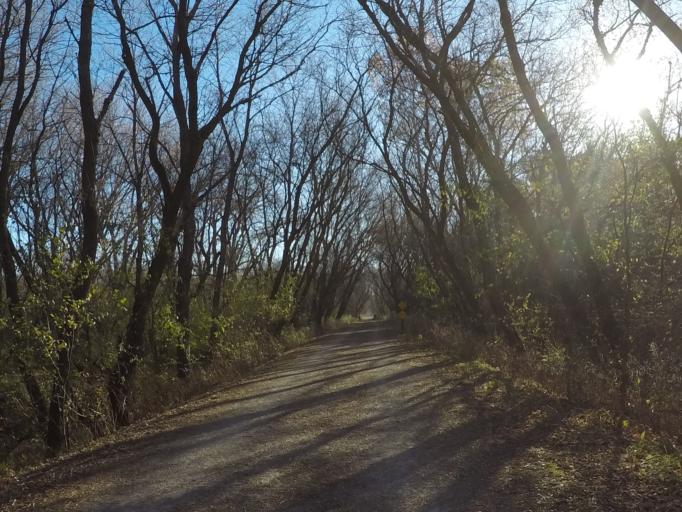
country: US
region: Wisconsin
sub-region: Dane County
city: Cottage Grove
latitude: 43.0741
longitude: -89.1683
